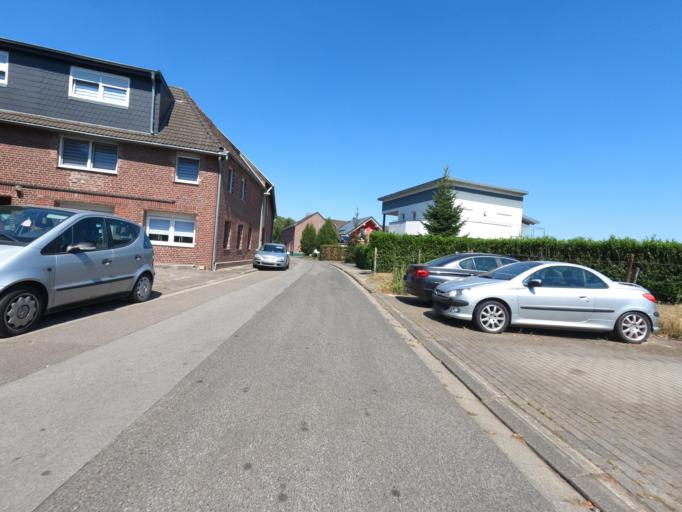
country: DE
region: North Rhine-Westphalia
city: Wegberg
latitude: 51.1050
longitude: 6.2512
